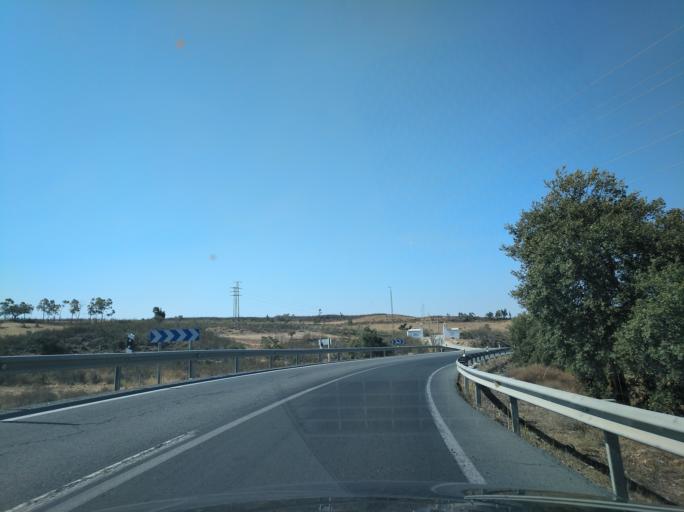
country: ES
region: Andalusia
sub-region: Provincia de Huelva
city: San Bartolome de la Torre
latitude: 37.4721
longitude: -7.1263
